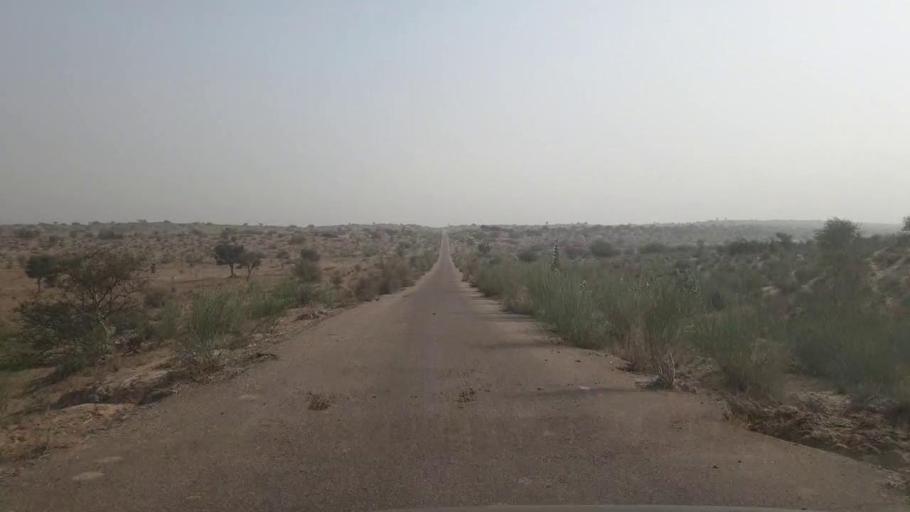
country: PK
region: Sindh
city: Chor
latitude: 25.5051
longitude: 69.9695
